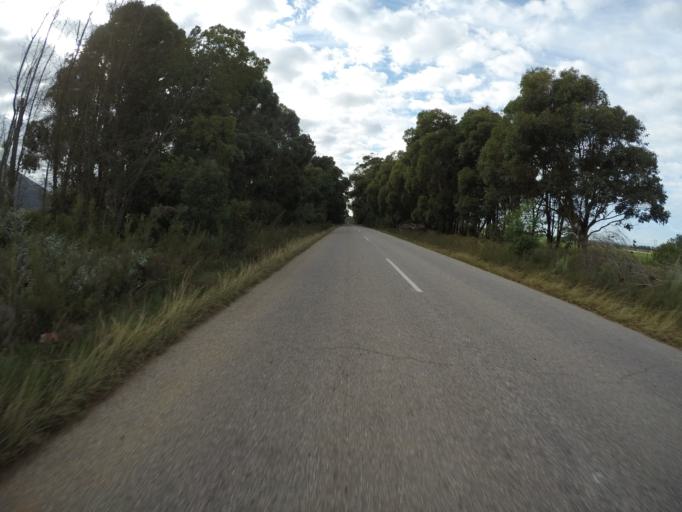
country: ZA
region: Eastern Cape
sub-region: Cacadu District Municipality
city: Kareedouw
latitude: -34.0458
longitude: 24.4506
